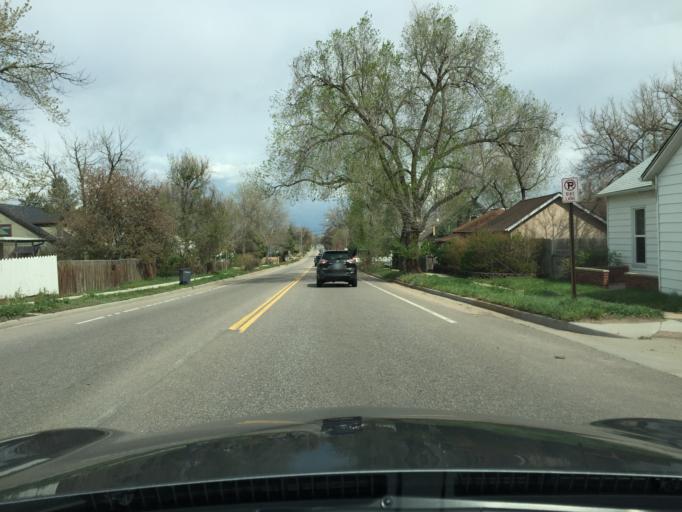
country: US
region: Colorado
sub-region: Boulder County
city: Lafayette
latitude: 40.0002
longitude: -105.0868
